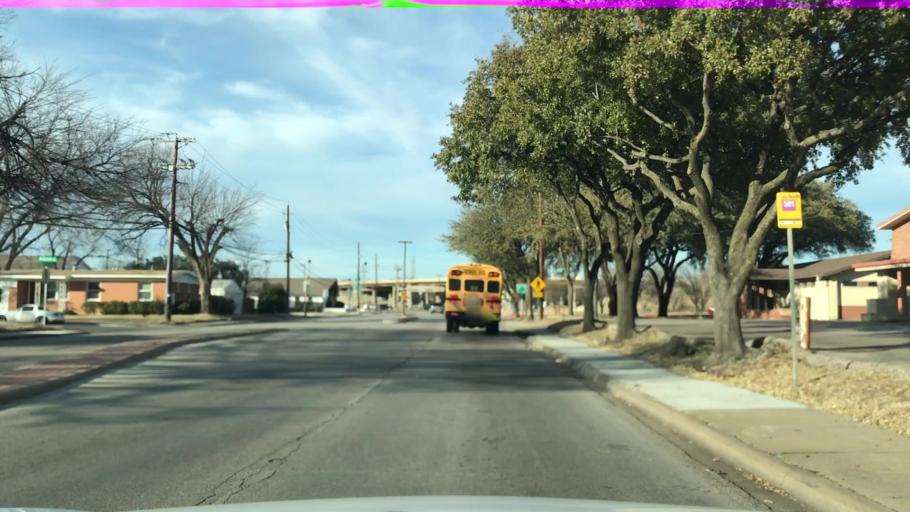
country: US
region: Texas
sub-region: Dallas County
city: Irving
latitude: 32.8127
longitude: -96.9599
